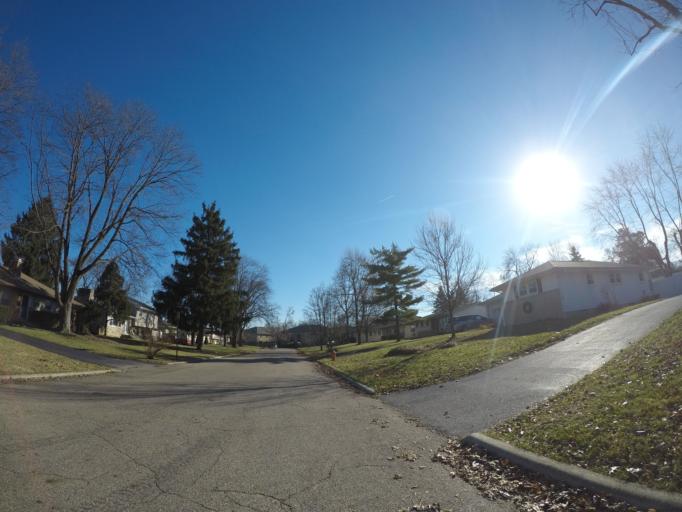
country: US
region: Ohio
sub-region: Franklin County
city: Upper Arlington
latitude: 40.0206
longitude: -83.0412
